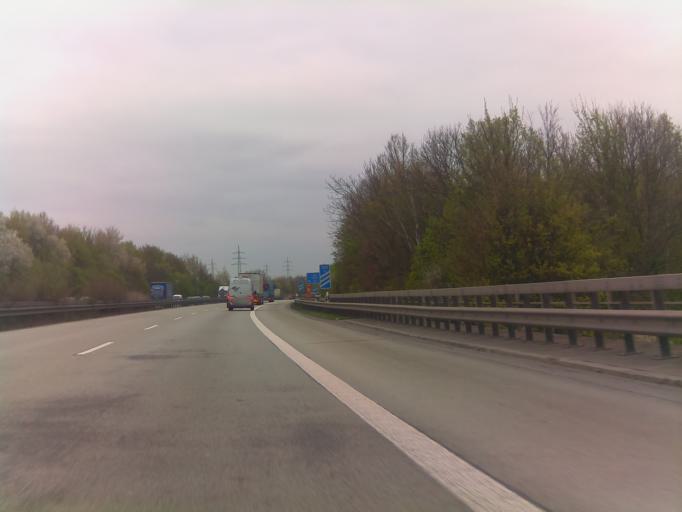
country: DE
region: Rheinland-Pfalz
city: Albig
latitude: 49.7635
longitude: 8.1147
